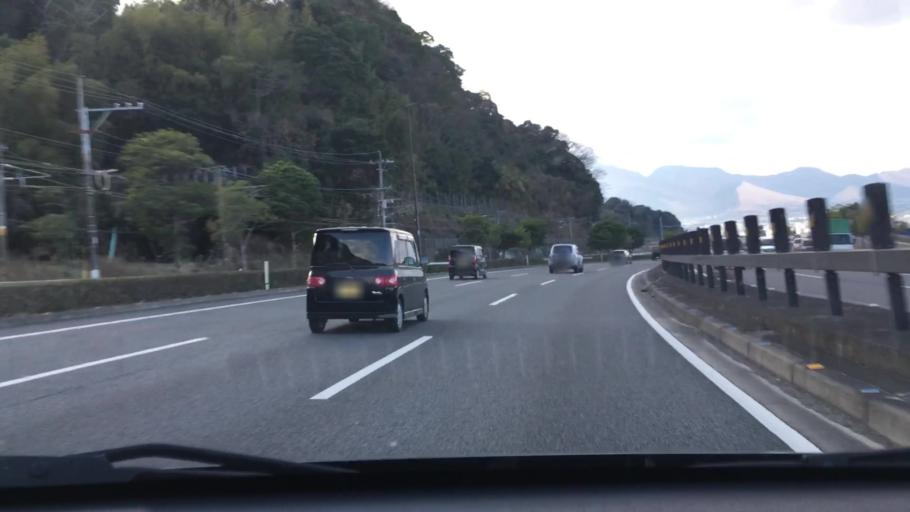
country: JP
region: Oita
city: Oita
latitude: 33.2509
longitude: 131.5711
